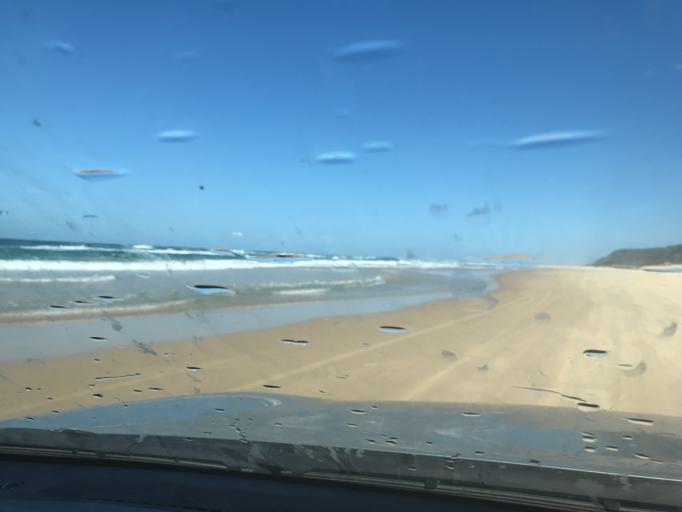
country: AU
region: Queensland
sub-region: Fraser Coast
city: Urangan
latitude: -25.1592
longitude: 153.2893
